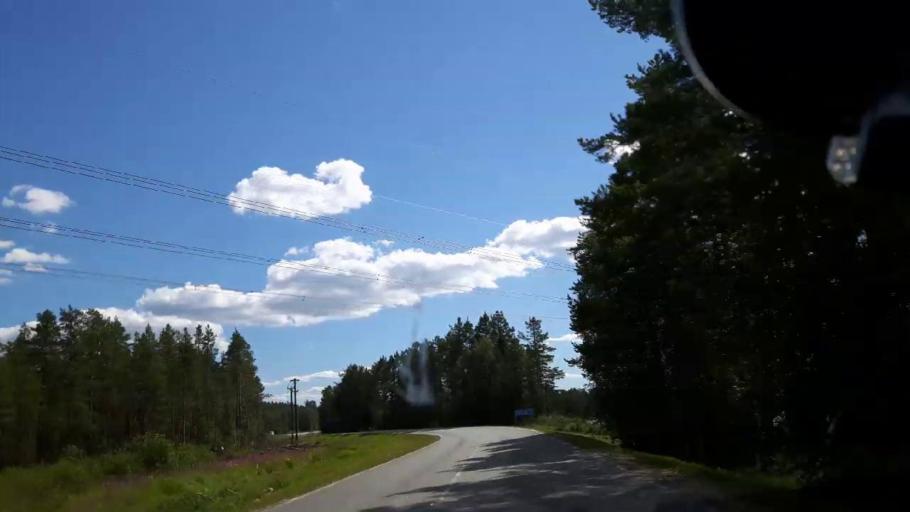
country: SE
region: Jaemtland
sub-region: Ragunda Kommun
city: Hammarstrand
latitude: 62.8772
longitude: 16.2210
